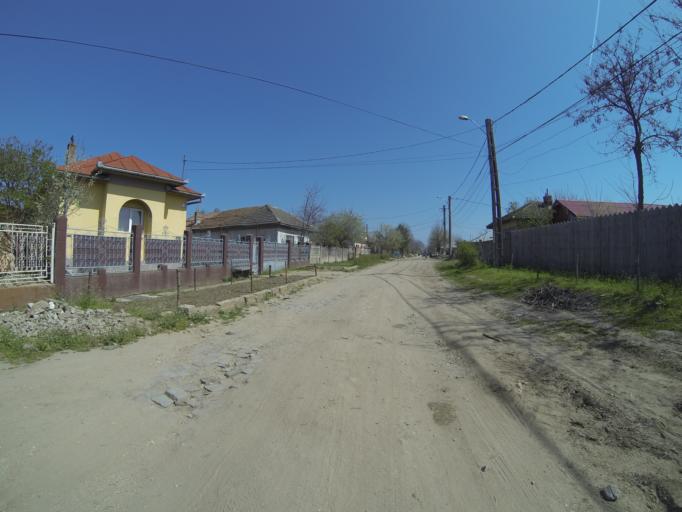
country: RO
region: Dolj
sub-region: Comuna Segarcea
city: Segarcea
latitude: 44.0996
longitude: 23.7305
